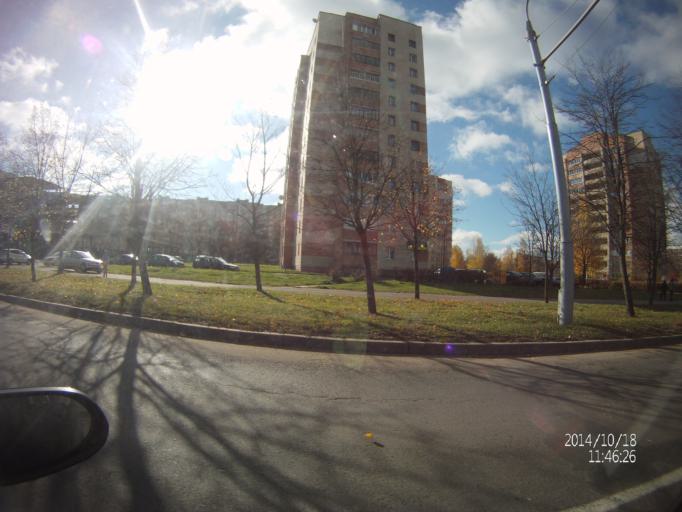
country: BY
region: Minsk
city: Novoye Medvezhino
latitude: 53.8721
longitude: 27.4717
